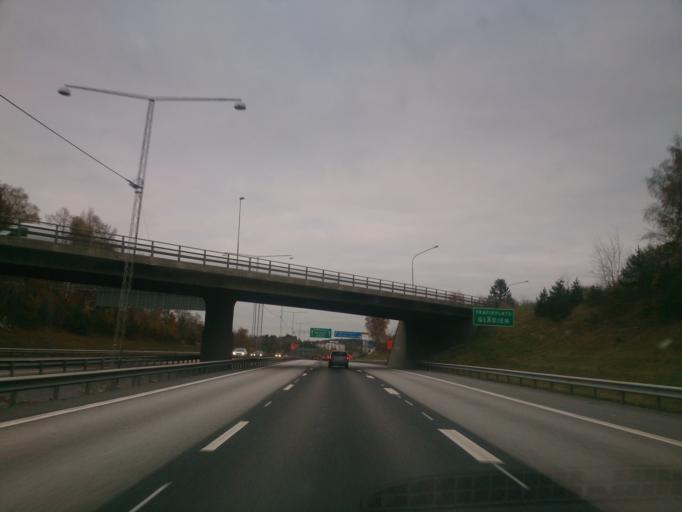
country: SE
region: Stockholm
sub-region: Upplands Vasby Kommun
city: Upplands Vaesby
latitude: 59.5052
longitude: 17.9251
